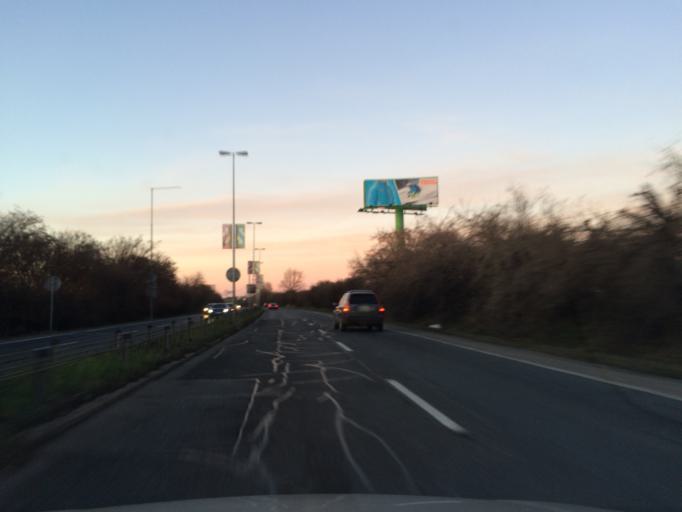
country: CZ
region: Central Bohemia
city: Tuchomerice
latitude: 50.1046
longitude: 14.2943
